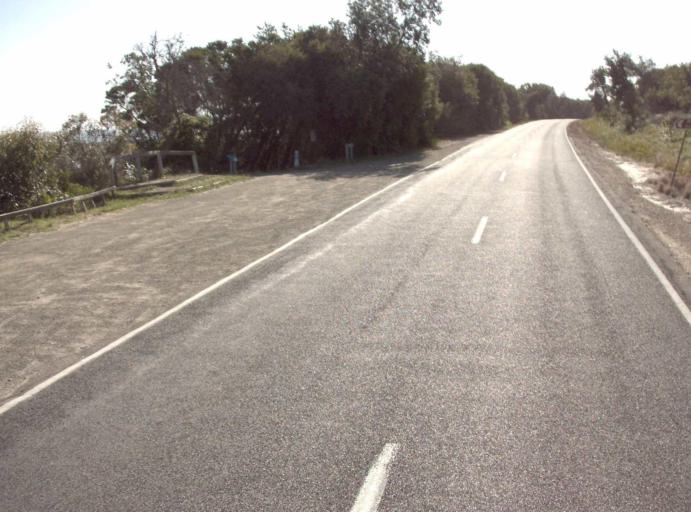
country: AU
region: Victoria
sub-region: East Gippsland
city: Lakes Entrance
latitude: -37.7986
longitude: 148.5795
